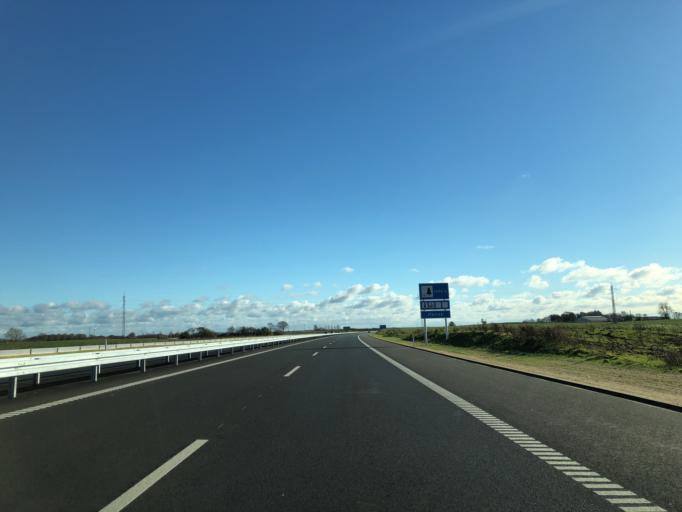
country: DK
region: Central Jutland
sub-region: Holstebro Kommune
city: Holstebro
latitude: 56.3770
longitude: 8.6969
